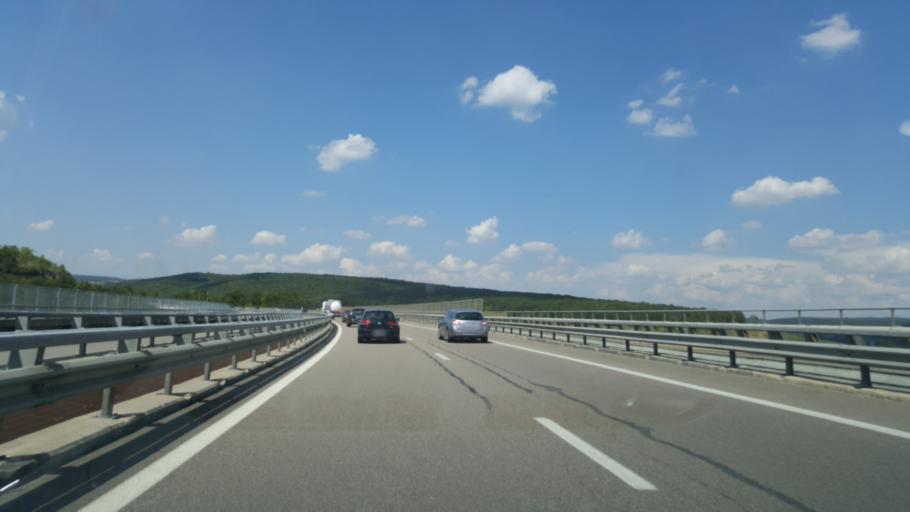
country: FR
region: Bourgogne
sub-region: Departement de la Cote-d'Or
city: Savigny-les-Beaune
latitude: 47.1639
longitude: 4.6985
